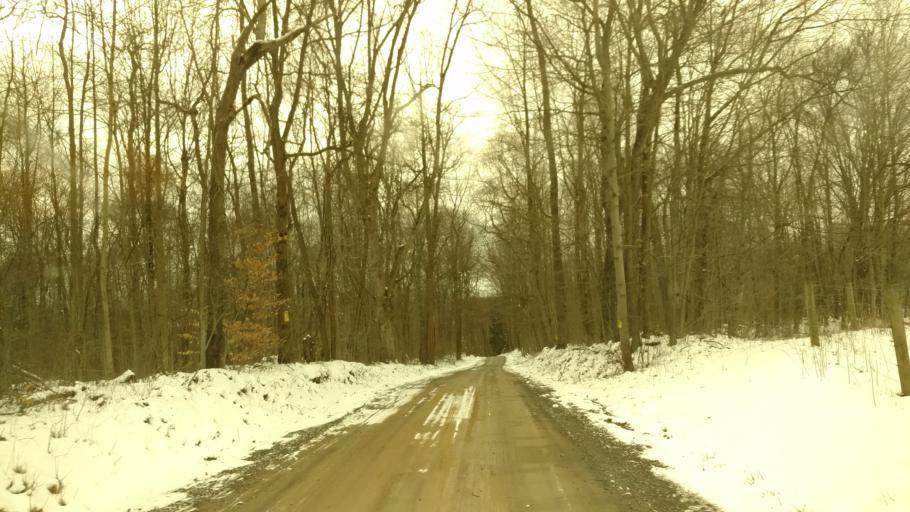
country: US
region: Pennsylvania
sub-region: Mercer County
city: Mercer
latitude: 41.3390
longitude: -80.2408
